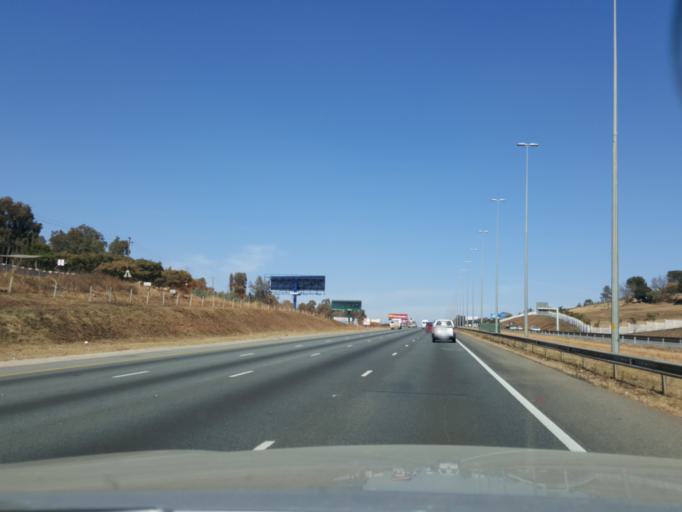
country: ZA
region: Gauteng
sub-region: City of Tshwane Metropolitan Municipality
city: Centurion
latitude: -25.8884
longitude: 28.2549
